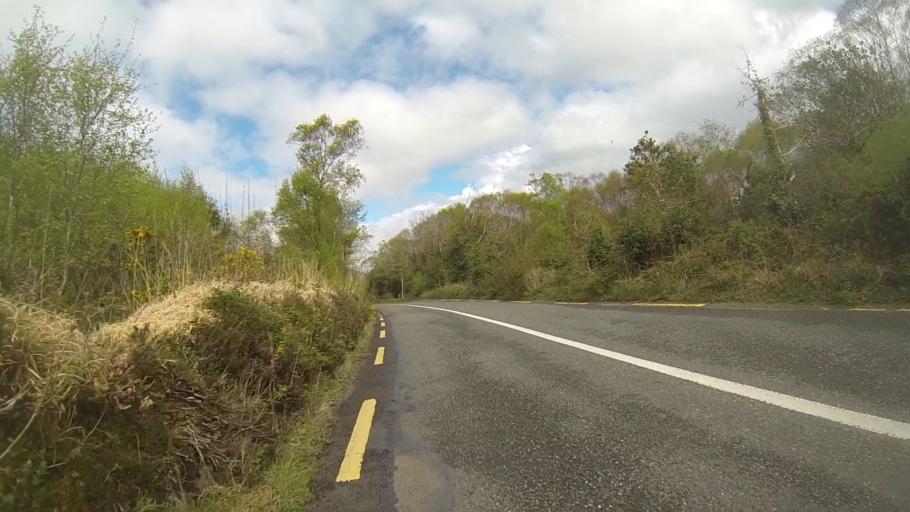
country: IE
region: Munster
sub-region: Ciarrai
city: Kenmare
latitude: 51.8247
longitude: -9.8553
